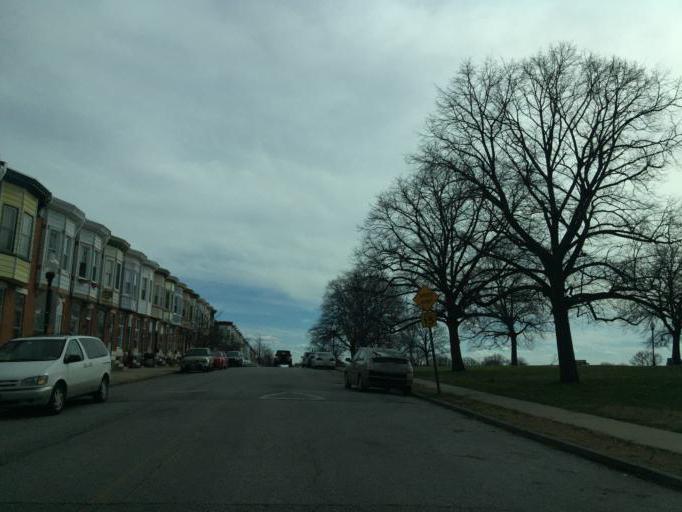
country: US
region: Maryland
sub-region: City of Baltimore
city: Baltimore
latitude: 39.2893
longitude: -76.5732
